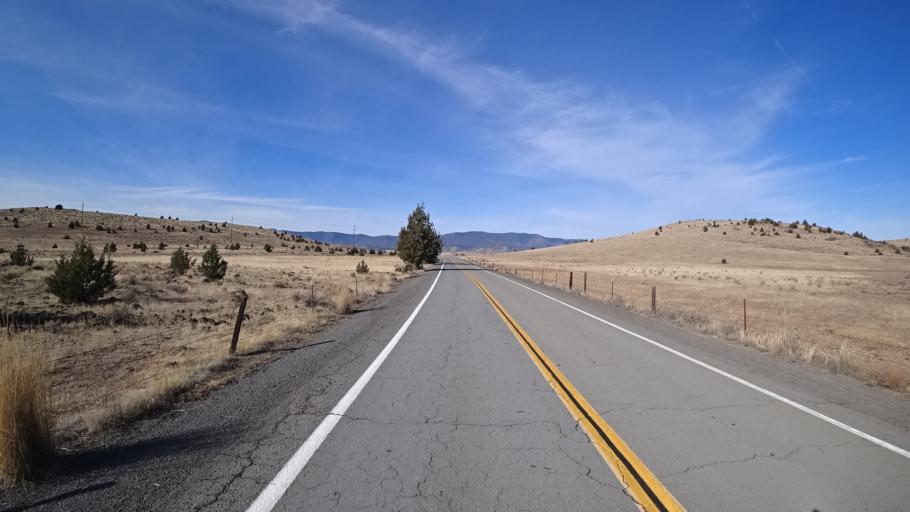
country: US
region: California
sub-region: Siskiyou County
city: Weed
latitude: 41.5537
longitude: -122.4780
